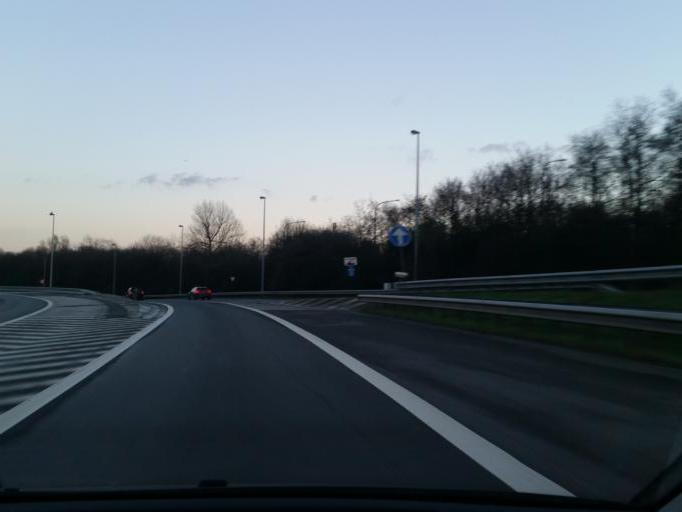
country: BE
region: Flanders
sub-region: Provincie Antwerpen
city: Antwerpen
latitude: 51.1975
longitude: 4.3784
